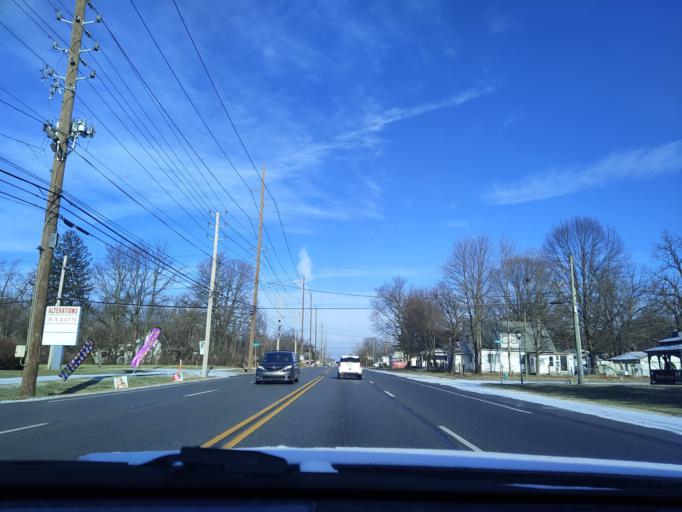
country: US
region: Indiana
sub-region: Marion County
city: Meridian Hills
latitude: 39.8886
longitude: -86.2115
